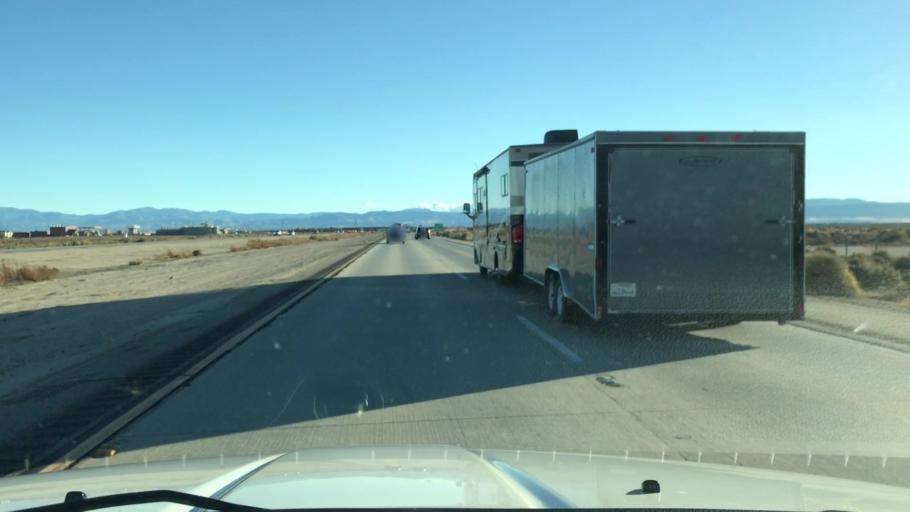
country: US
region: California
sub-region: Kern County
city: Rosamond
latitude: 34.7886
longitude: -118.1710
